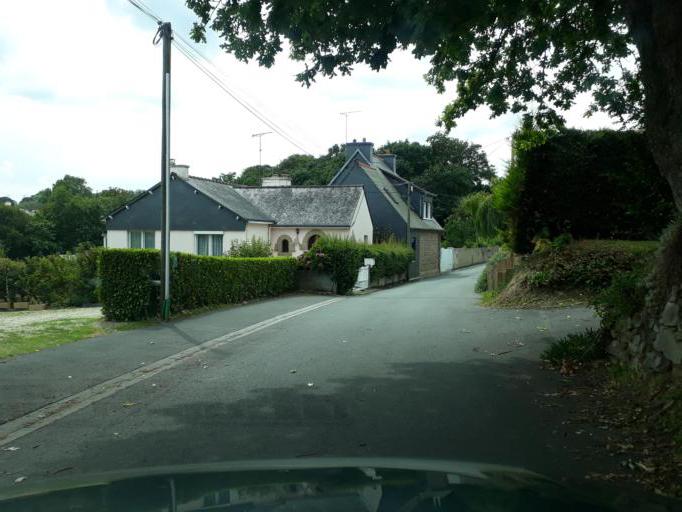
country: FR
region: Brittany
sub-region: Departement des Cotes-d'Armor
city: Paimpol
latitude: 48.7870
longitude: -3.0529
